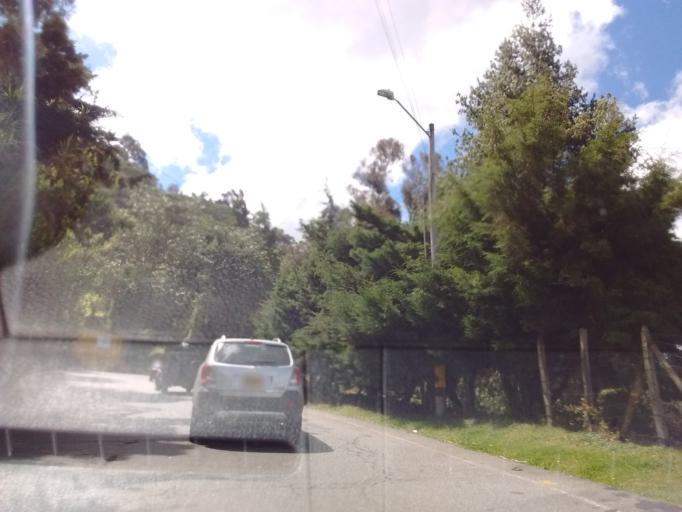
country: CO
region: Antioquia
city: Medellin
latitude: 6.2435
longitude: -75.5136
